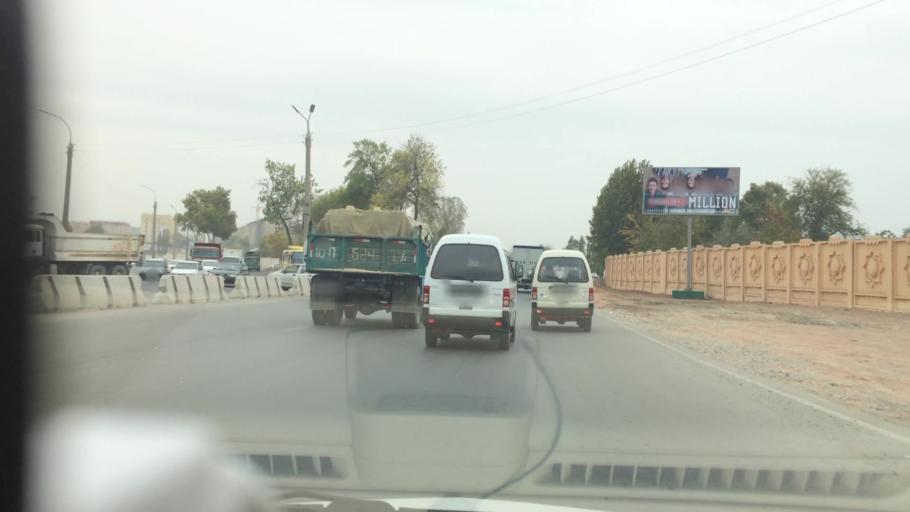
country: UZ
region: Toshkent
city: Salor
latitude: 41.3038
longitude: 69.3426
